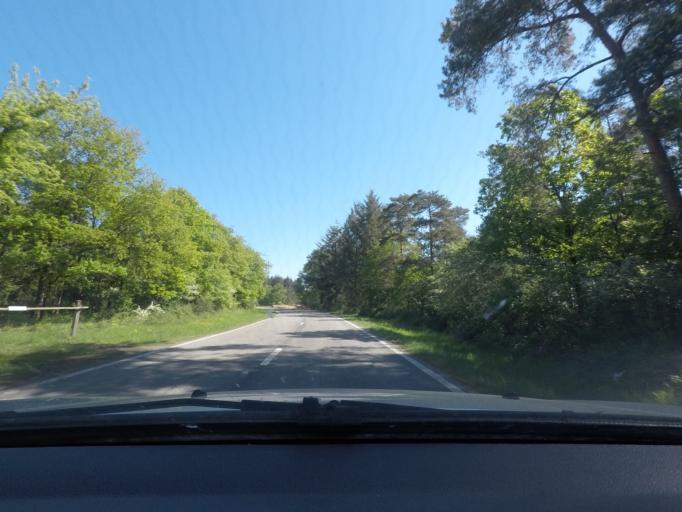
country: BE
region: Wallonia
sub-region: Province du Luxembourg
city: Wellin
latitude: 50.1735
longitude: 5.1167
